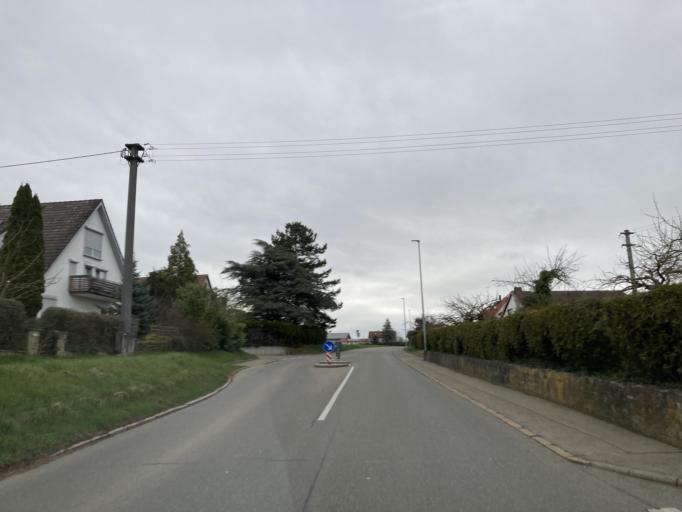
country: DE
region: Baden-Wuerttemberg
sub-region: Regierungsbezirk Stuttgart
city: Bondorf
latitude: 48.5086
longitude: 8.8731
